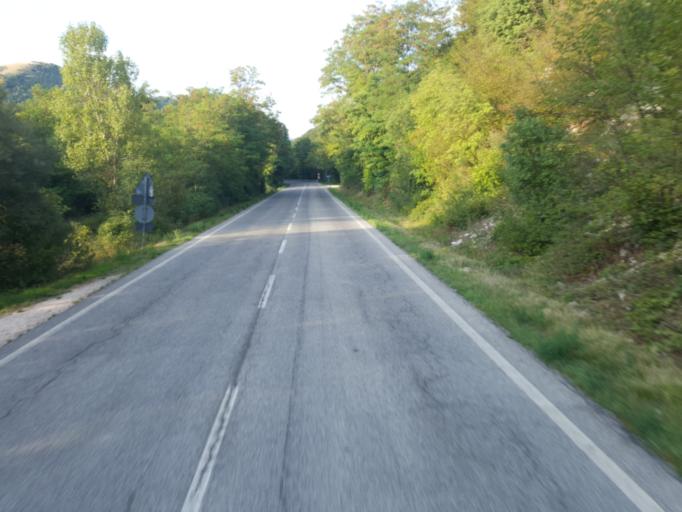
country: IT
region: The Marches
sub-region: Provincia di Ancona
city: Fabriano
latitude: 43.3186
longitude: 12.8381
